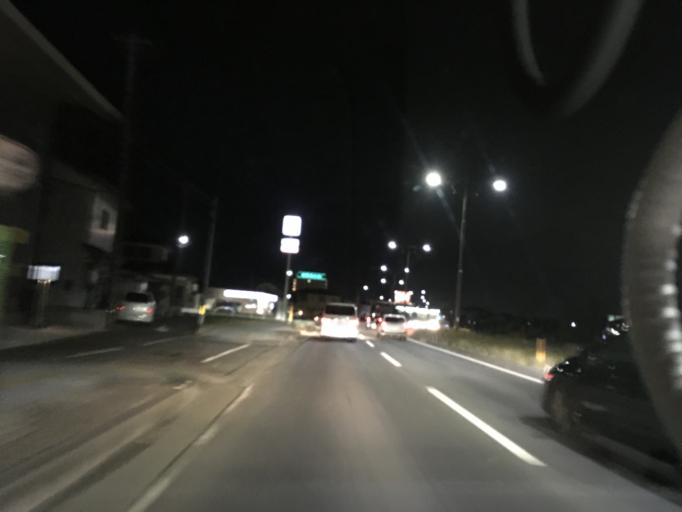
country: JP
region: Miyagi
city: Ishinomaki
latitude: 38.4430
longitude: 141.2770
